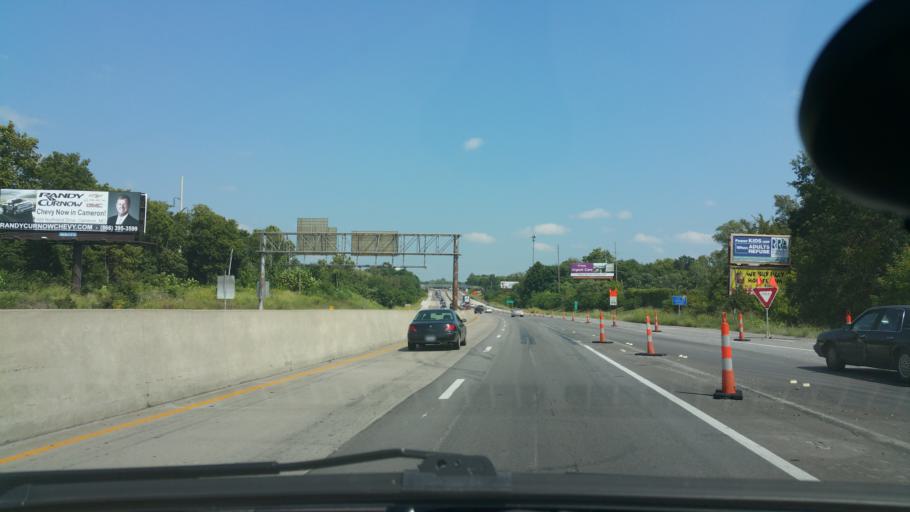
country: US
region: Missouri
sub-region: Clay County
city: Claycomo
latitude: 39.2075
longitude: -94.4881
